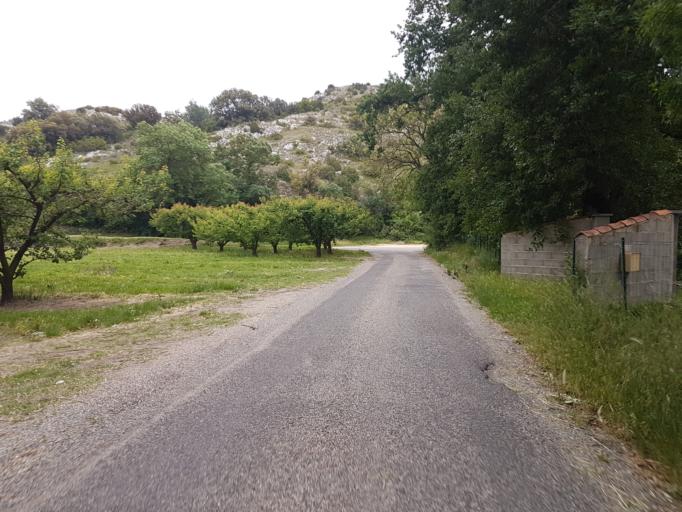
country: FR
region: Languedoc-Roussillon
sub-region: Departement du Gard
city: Sauveterre
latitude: 44.0341
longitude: 4.7828
